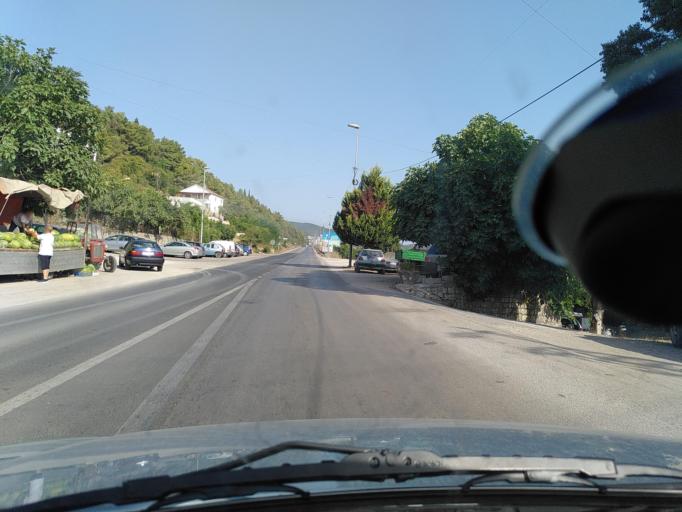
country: ME
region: Ulcinj
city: Ulcinj
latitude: 41.9381
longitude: 19.2177
